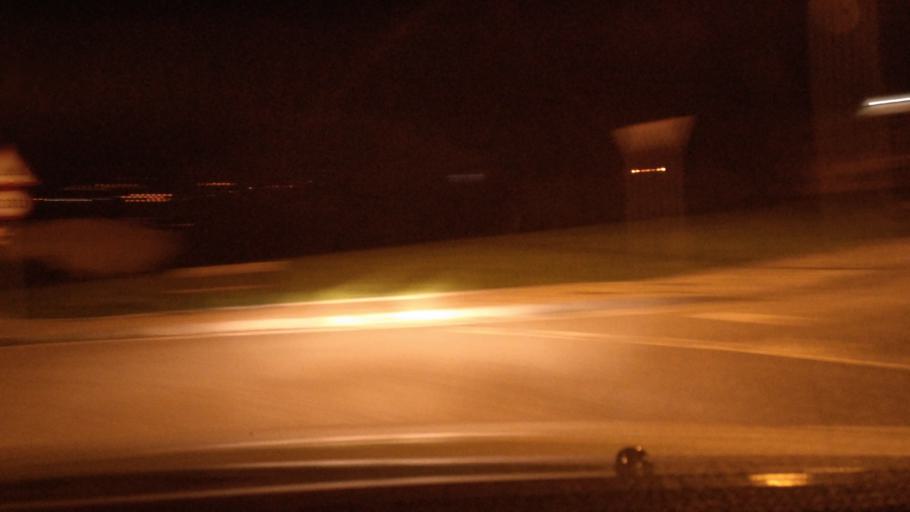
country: ES
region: Galicia
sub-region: Provincia de Pontevedra
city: Moana
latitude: 42.2888
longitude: -8.7276
